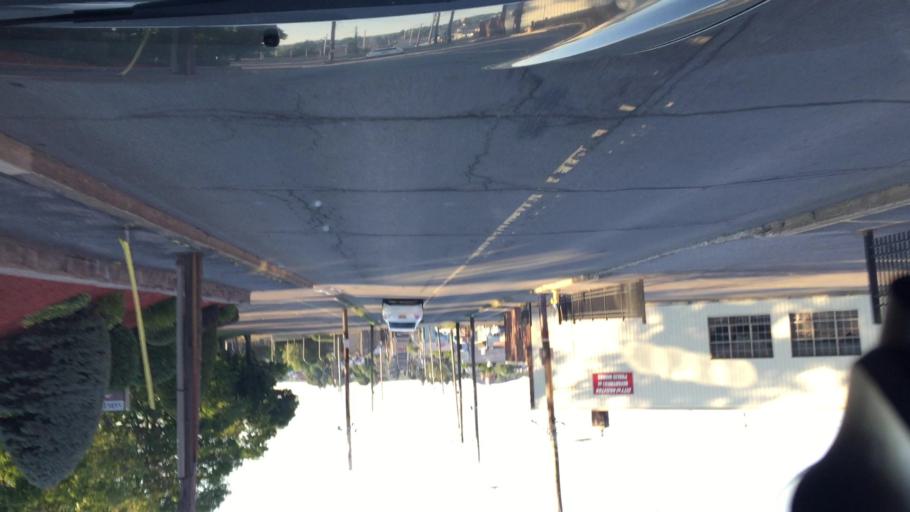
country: US
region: Pennsylvania
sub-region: Luzerne County
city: Hazleton
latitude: 40.9591
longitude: -75.9681
